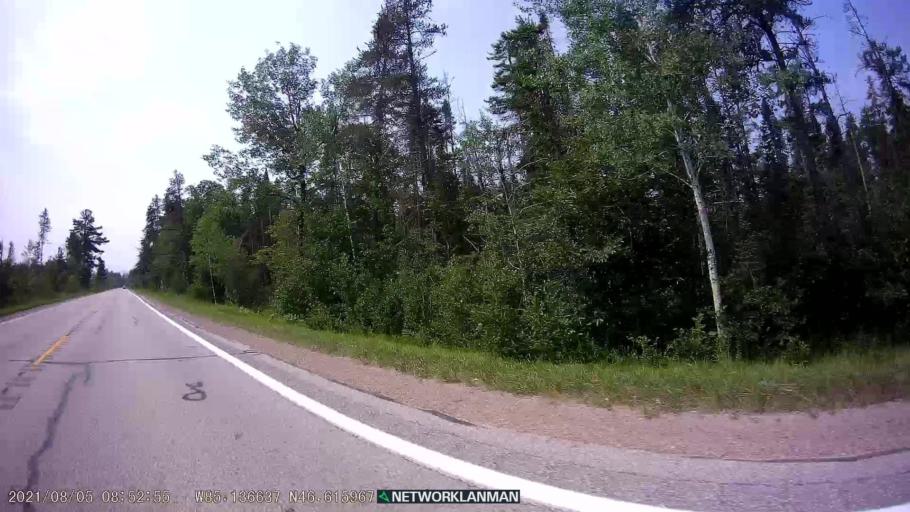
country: US
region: Michigan
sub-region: Luce County
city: Newberry
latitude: 46.6155
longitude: -85.1368
